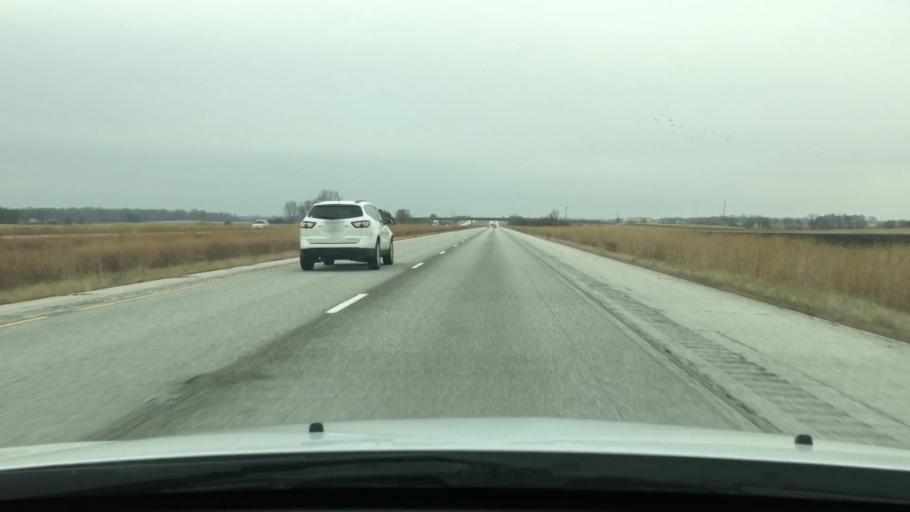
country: US
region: Illinois
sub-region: Morgan County
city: South Jacksonville
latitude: 39.6964
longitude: -90.1944
